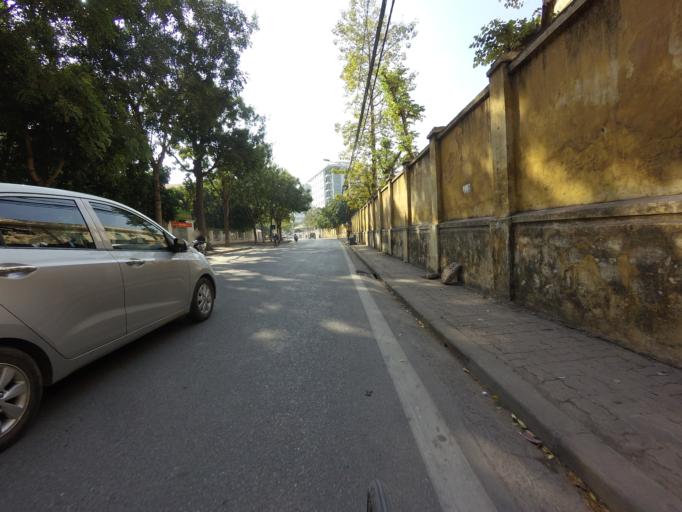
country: VN
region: Ha Noi
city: Hanoi
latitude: 21.0424
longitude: 105.8314
